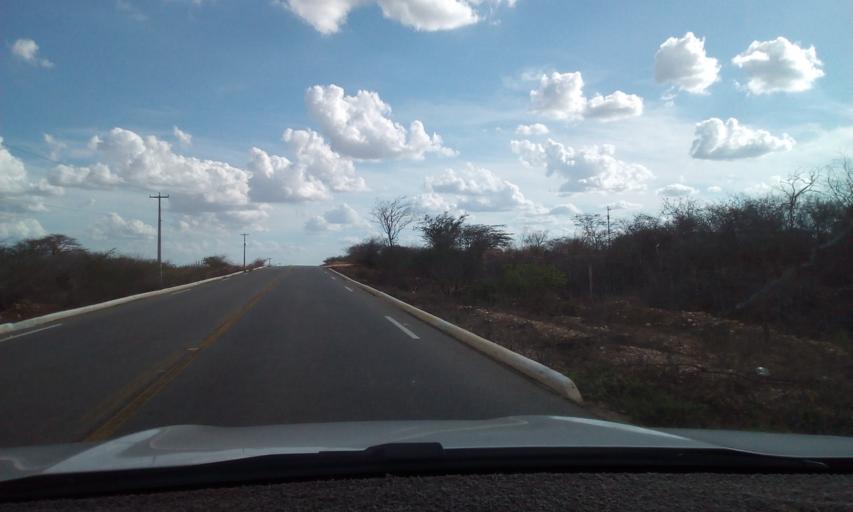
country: BR
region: Paraiba
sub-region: Soledade
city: Soledade
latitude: -6.8098
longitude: -36.4039
